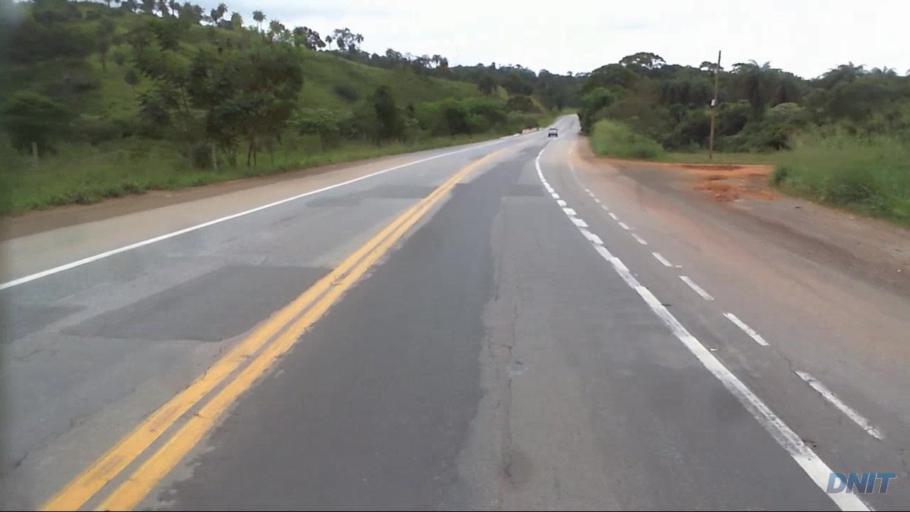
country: BR
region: Minas Gerais
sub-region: Barao De Cocais
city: Barao de Cocais
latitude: -19.8159
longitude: -43.3964
